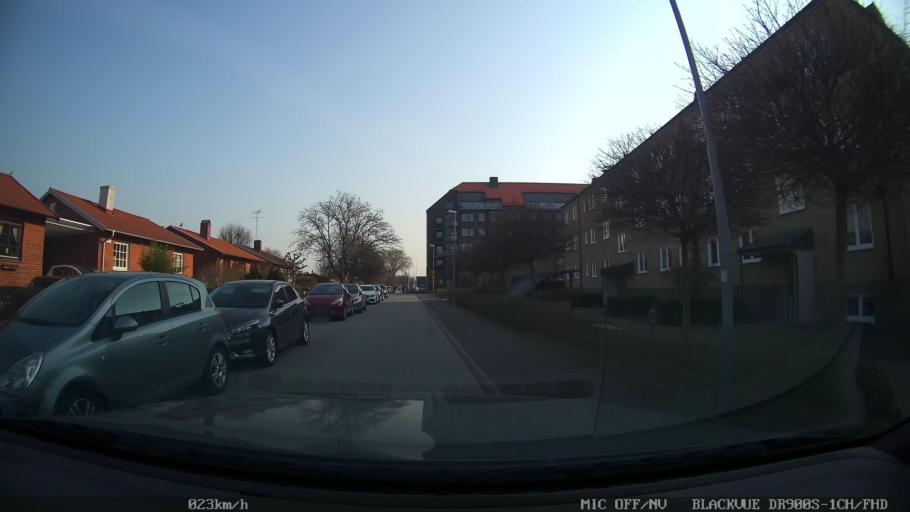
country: SE
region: Skane
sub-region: Ystads Kommun
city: Ystad
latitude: 55.4372
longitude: 13.8304
